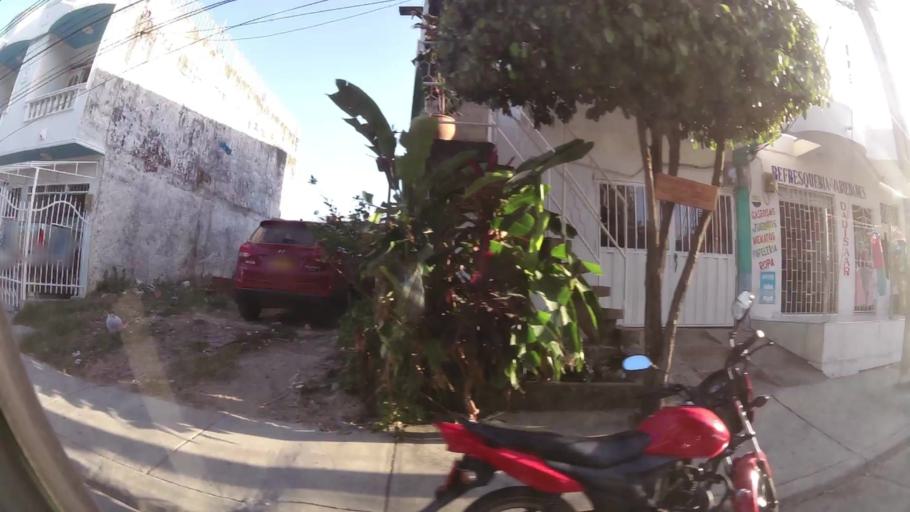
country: CO
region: Bolivar
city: Cartagena
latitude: 10.3976
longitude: -75.4763
